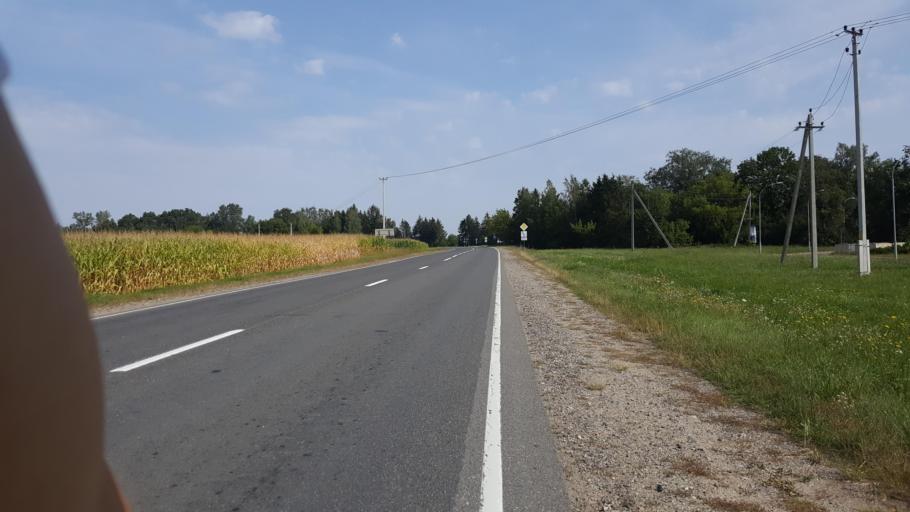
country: BY
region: Brest
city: Kamyanyets
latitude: 52.4102
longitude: 23.7873
